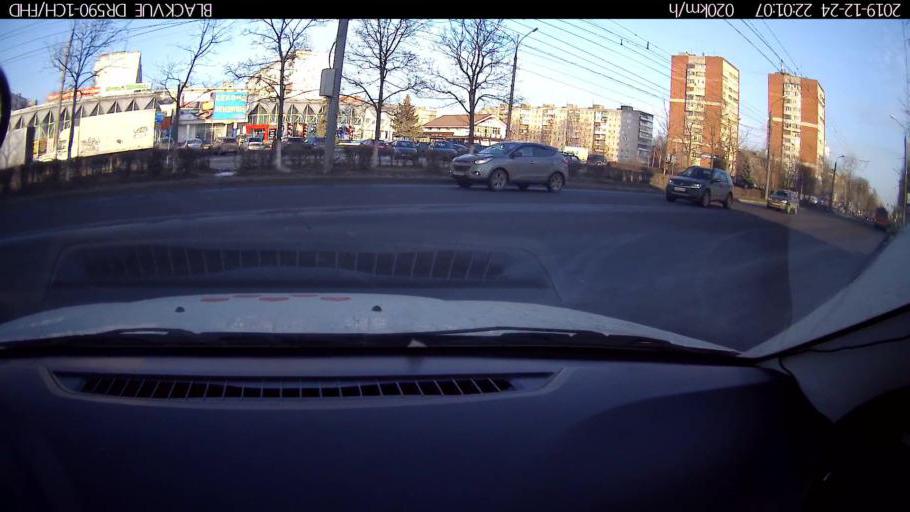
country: RU
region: Nizjnij Novgorod
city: Burevestnik
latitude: 56.2272
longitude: 43.8651
